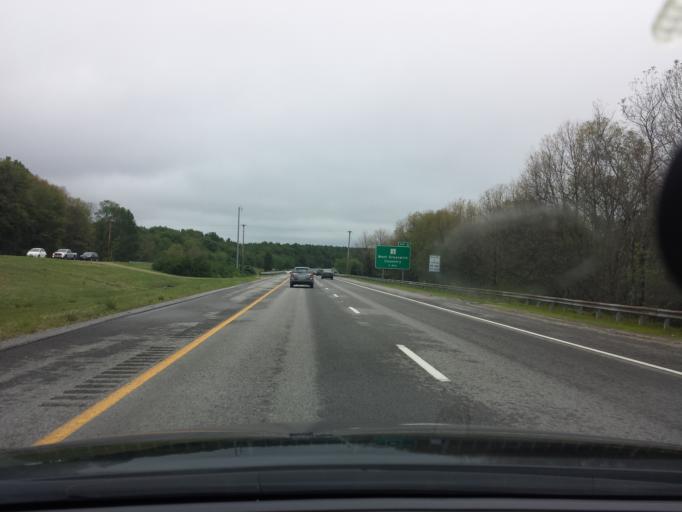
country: US
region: Rhode Island
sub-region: Kent County
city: West Greenwich
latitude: 41.6382
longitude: -71.6261
